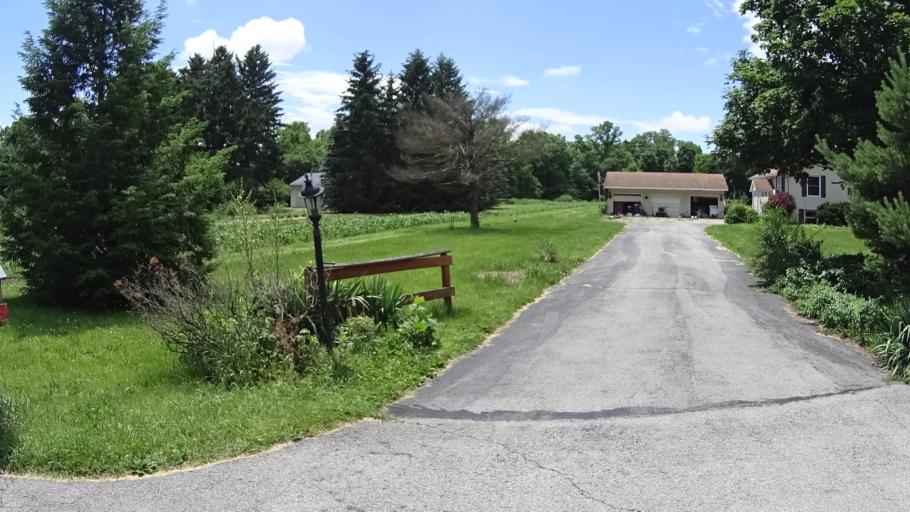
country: US
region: Ohio
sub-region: Erie County
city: Milan
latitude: 41.3020
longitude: -82.5987
